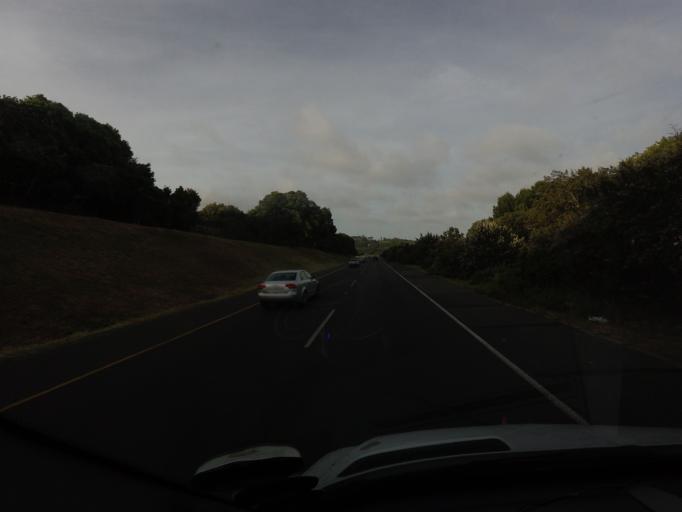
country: ZA
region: Western Cape
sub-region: City of Cape Town
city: Bergvliet
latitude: -34.0204
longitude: 18.4512
